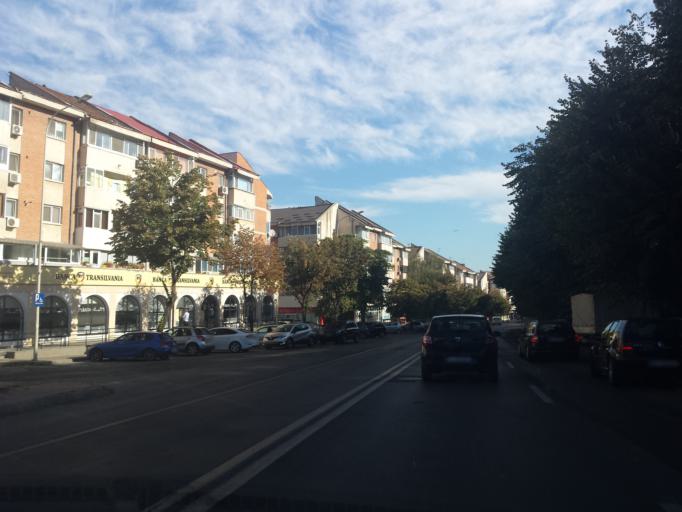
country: RO
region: Tulcea
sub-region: Municipiul Tulcea
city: Tulcea
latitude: 45.1711
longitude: 28.7979
